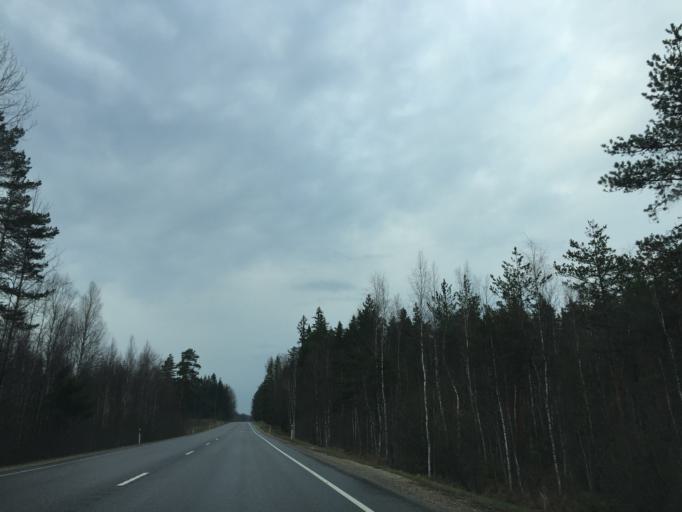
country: EE
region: Vorumaa
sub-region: Antsla vald
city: Vana-Antsla
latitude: 58.0219
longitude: 26.7430
